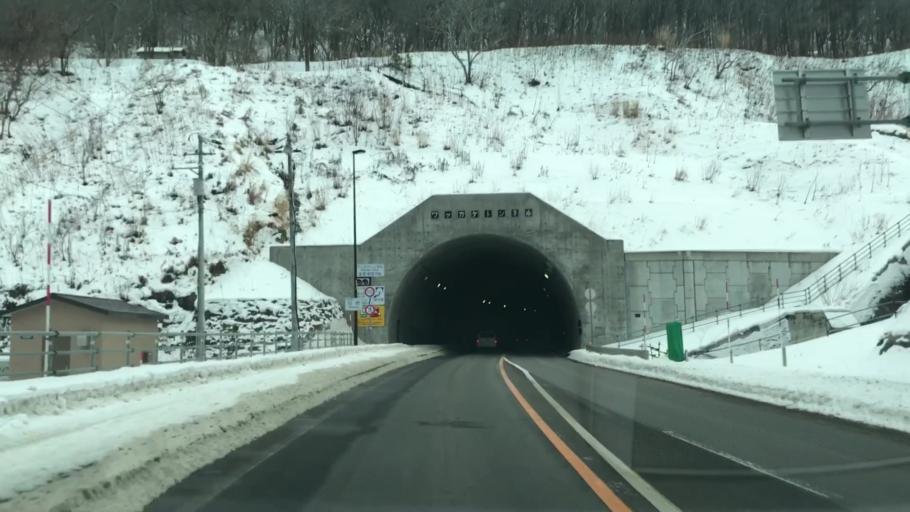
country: JP
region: Hokkaido
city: Yoichi
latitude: 43.2410
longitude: 140.7297
